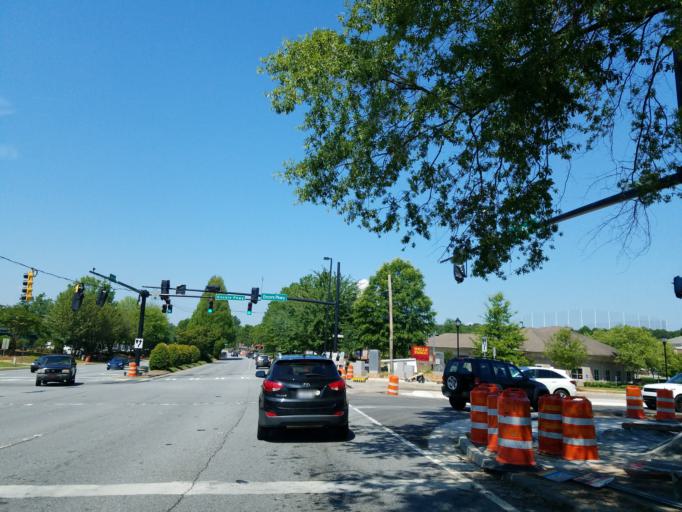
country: US
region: Georgia
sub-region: Fulton County
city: Alpharetta
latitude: 34.0442
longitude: -84.2993
